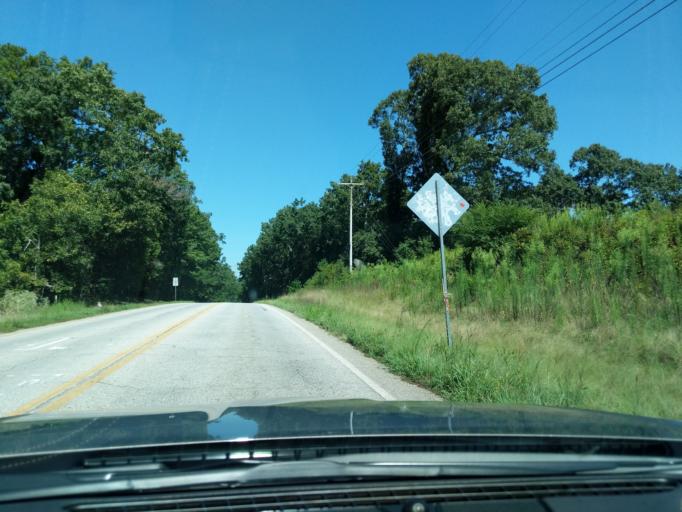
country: US
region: Georgia
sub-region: Habersham County
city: Demorest
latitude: 34.5832
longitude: -83.6146
